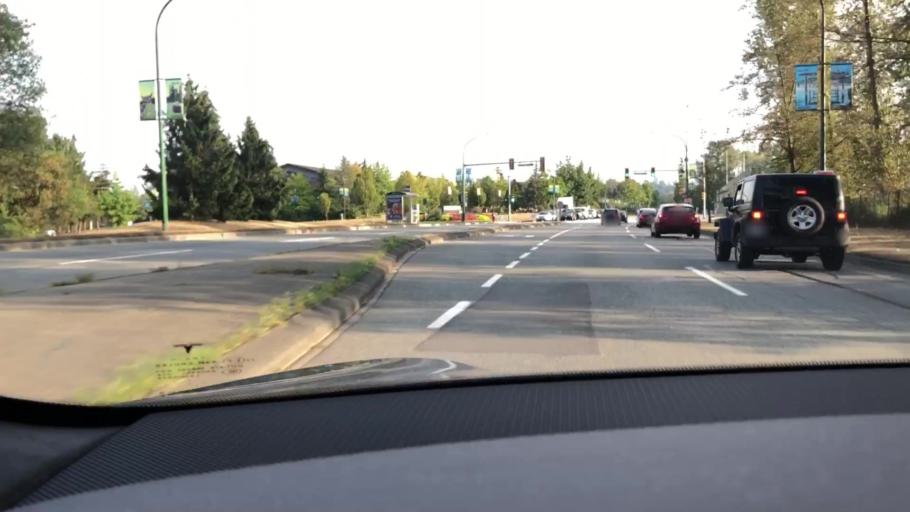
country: CA
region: British Columbia
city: Burnaby
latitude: 49.2543
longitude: -122.9666
